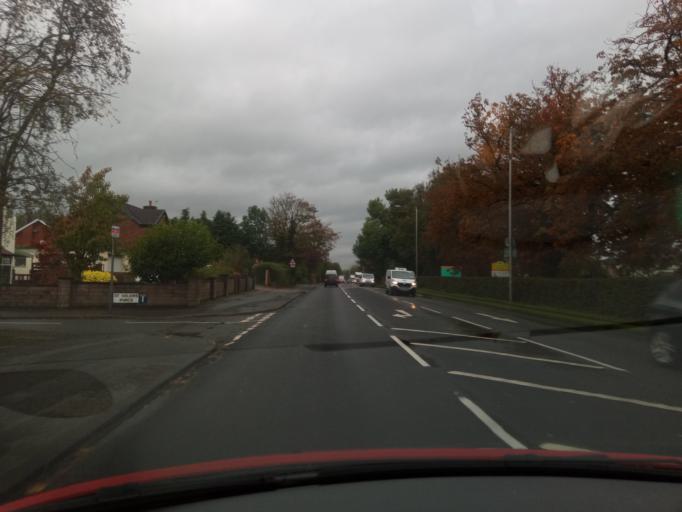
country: GB
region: England
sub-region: Lancashire
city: Catterall
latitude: 53.8309
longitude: -2.7379
